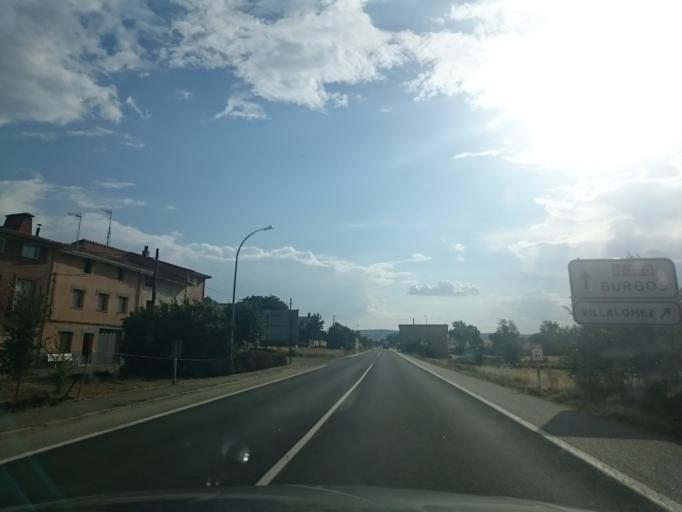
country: ES
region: Castille and Leon
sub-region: Provincia de Burgos
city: Tosantos
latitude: 42.4135
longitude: -3.2448
